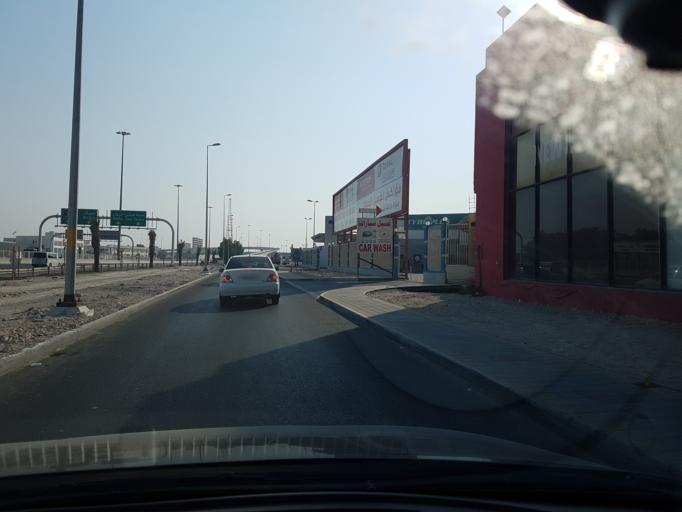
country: BH
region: Northern
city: Sitrah
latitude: 26.1287
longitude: 50.5979
